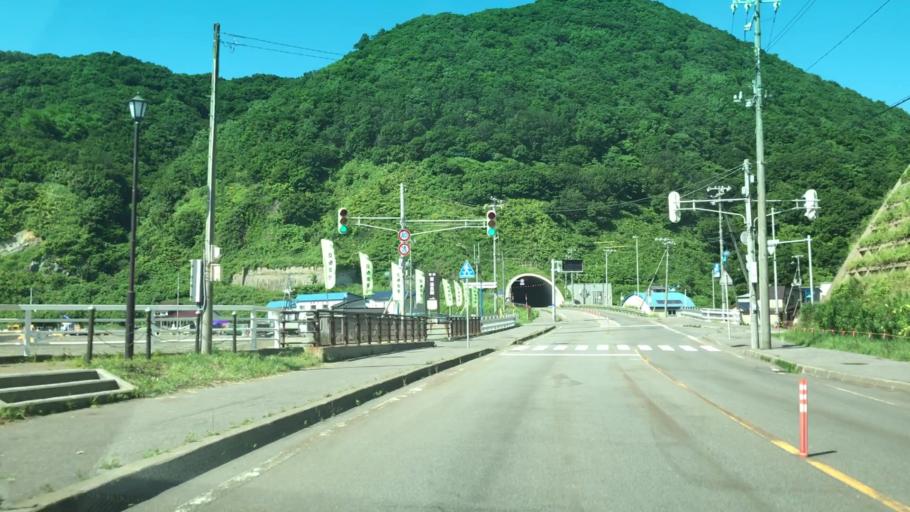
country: JP
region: Hokkaido
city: Iwanai
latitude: 43.1120
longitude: 140.4504
